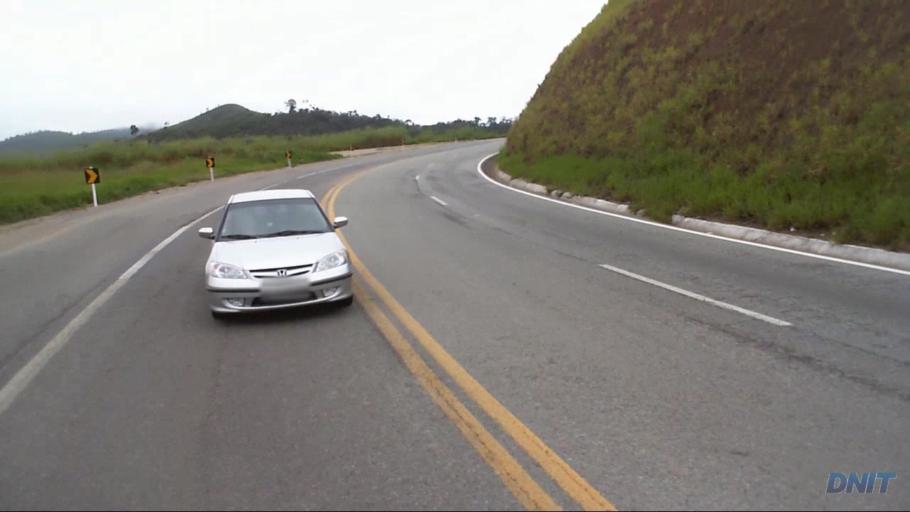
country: BR
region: Minas Gerais
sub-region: Nova Era
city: Nova Era
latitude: -19.6423
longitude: -42.9042
